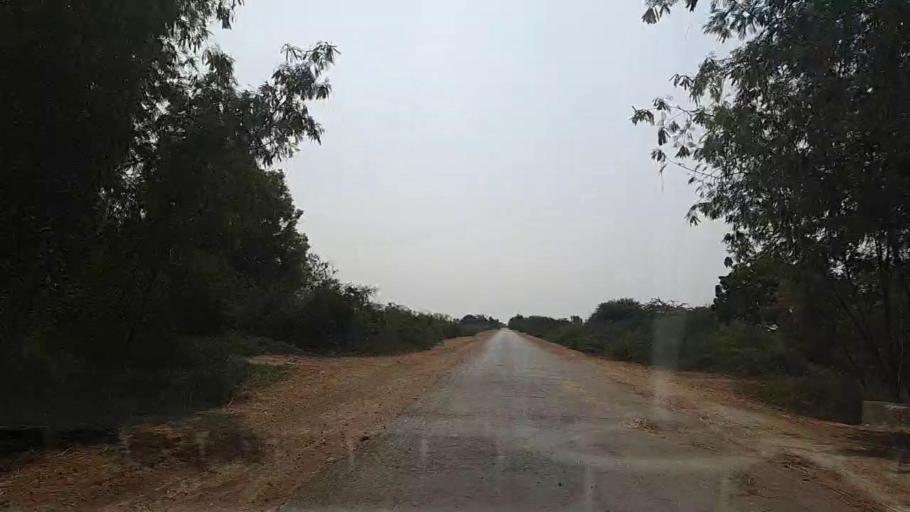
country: PK
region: Sindh
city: Chuhar Jamali
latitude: 24.2613
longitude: 67.9083
